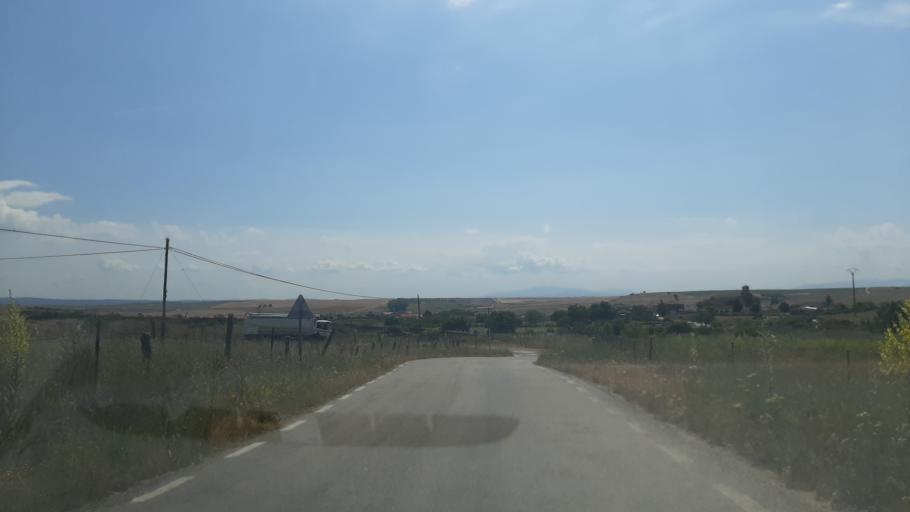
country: ES
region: Castille and Leon
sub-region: Provincia de Salamanca
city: Gallegos de Arganan
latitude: 40.6340
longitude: -6.7111
